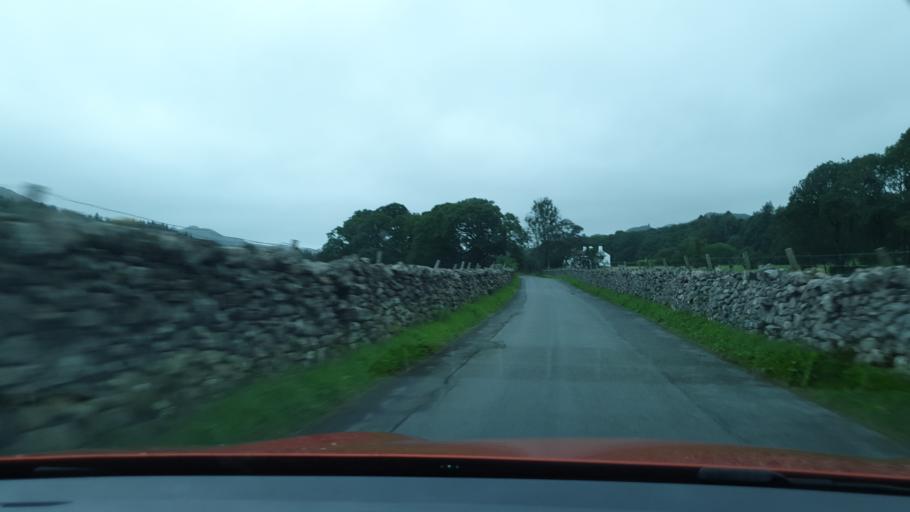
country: GB
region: England
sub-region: Cumbria
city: Seascale
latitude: 54.3880
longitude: -3.3084
